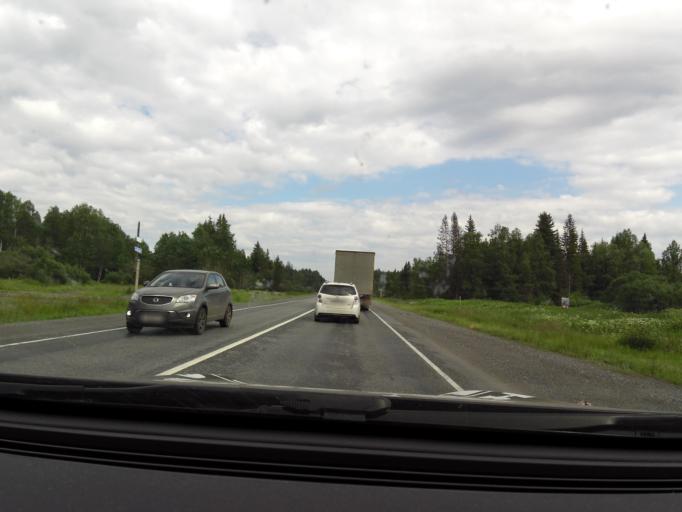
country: RU
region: Sverdlovsk
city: Nizhniye Sergi
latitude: 56.8240
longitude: 59.2908
